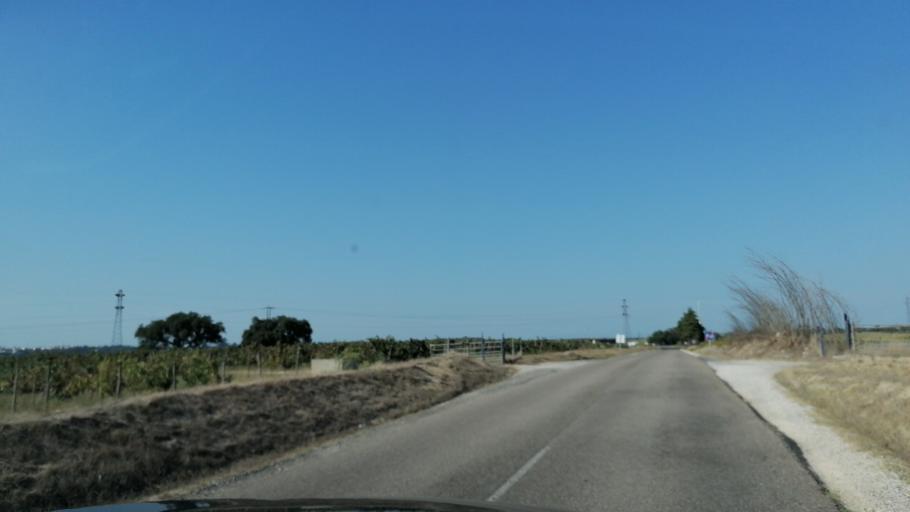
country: PT
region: Santarem
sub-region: Coruche
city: Coruche
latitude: 38.9336
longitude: -8.5178
